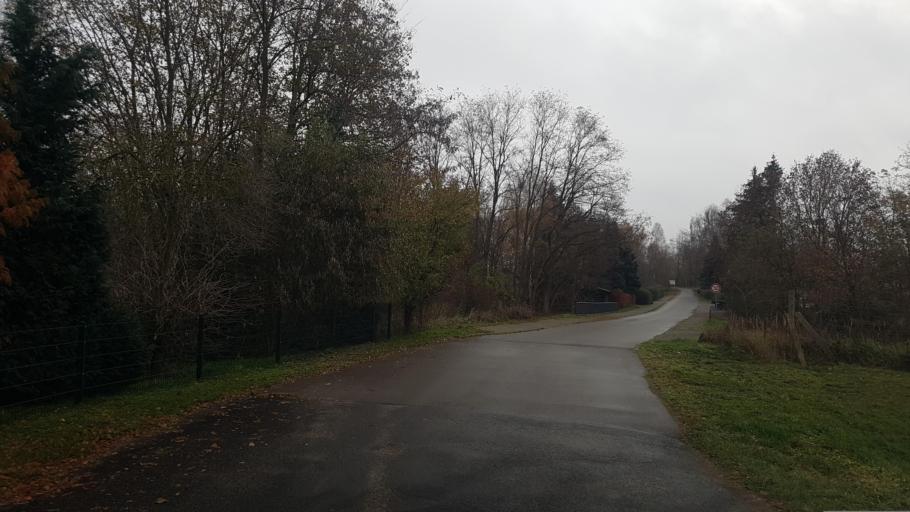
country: DE
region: Brandenburg
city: Lubbenau
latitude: 51.8295
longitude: 13.9272
